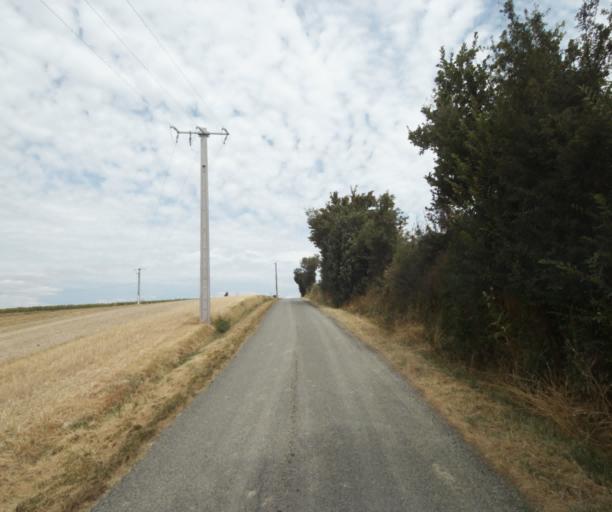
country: FR
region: Midi-Pyrenees
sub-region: Departement de la Haute-Garonne
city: Saint-Felix-Lauragais
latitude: 43.4104
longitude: 1.9048
